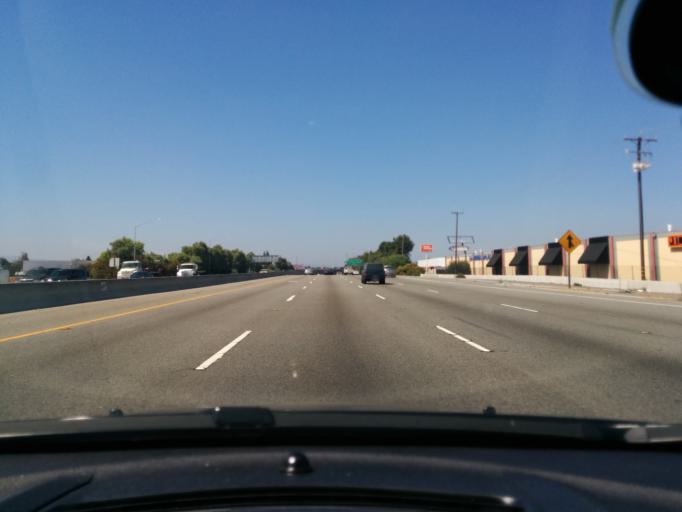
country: US
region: California
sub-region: Santa Clara County
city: Santa Clara
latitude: 37.3771
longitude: -121.9428
